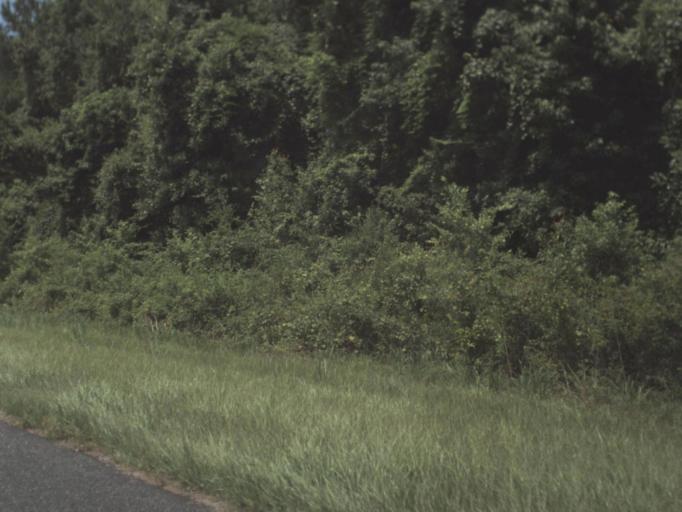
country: US
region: Florida
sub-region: Taylor County
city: Perry
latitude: 30.2824
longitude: -83.7291
